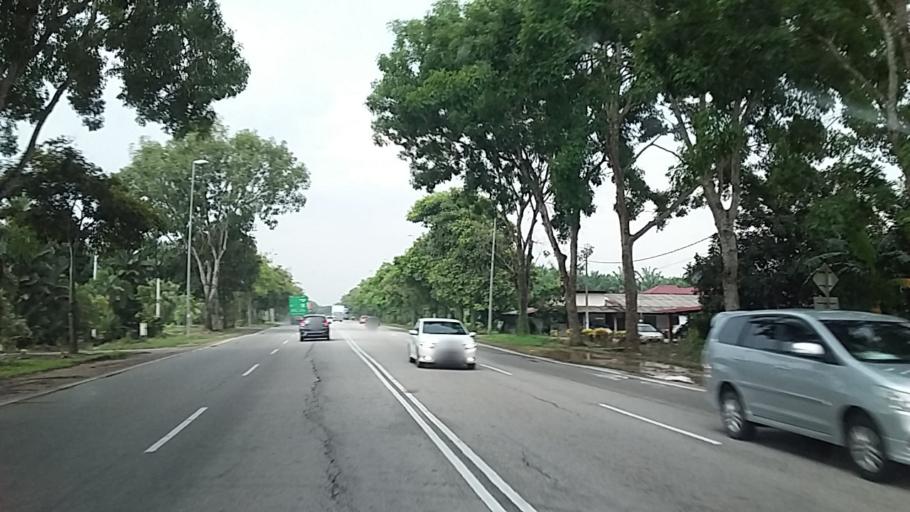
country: MY
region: Johor
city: Parit Raja
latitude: 1.8725
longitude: 103.1333
